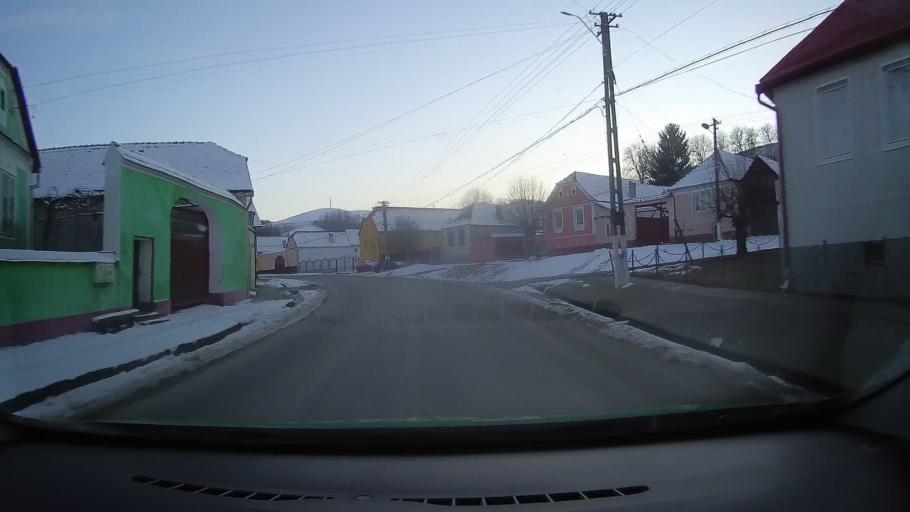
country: RO
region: Sibiu
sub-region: Comuna Brateiu
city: Brateiu
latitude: 46.1969
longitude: 24.4433
